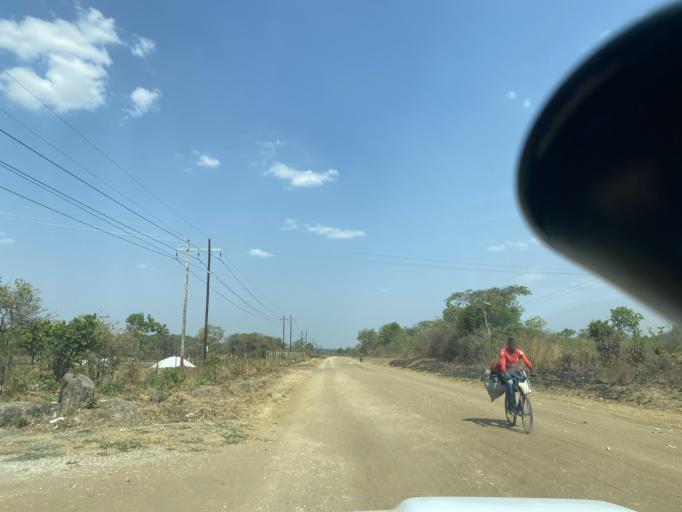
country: ZM
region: Lusaka
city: Lusaka
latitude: -15.3127
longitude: 28.0525
